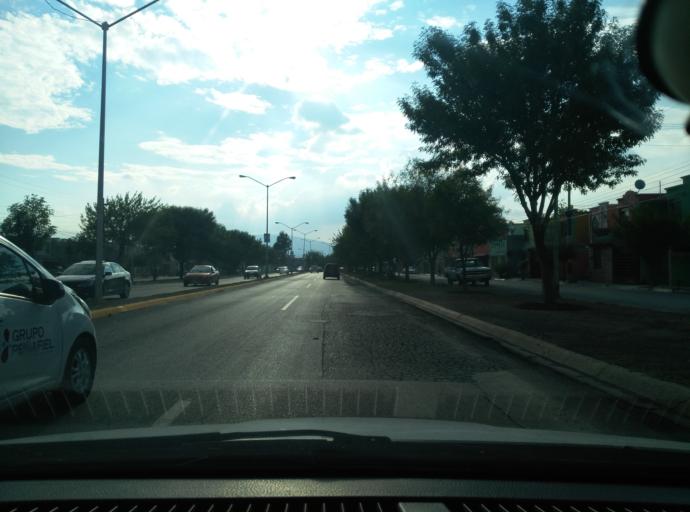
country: MX
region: Nuevo Leon
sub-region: Apodaca
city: Fraccionamiento Cosmopolis Octavo Sector
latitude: 25.7679
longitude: -100.2443
